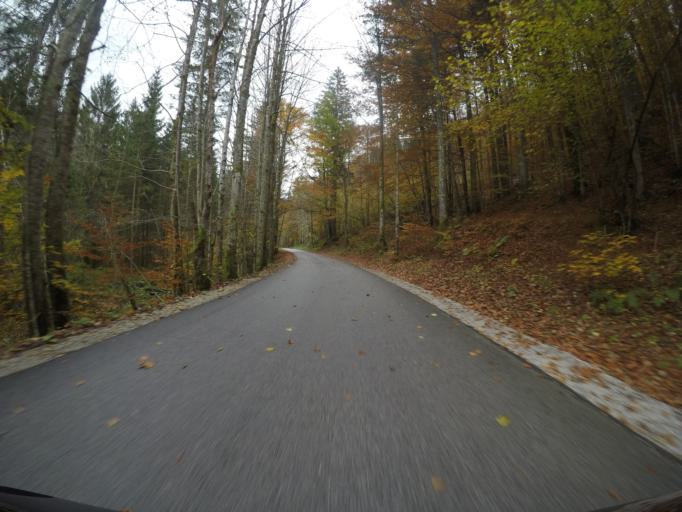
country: SI
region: Jesenice
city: Hrusica
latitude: 46.4197
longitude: 13.9790
